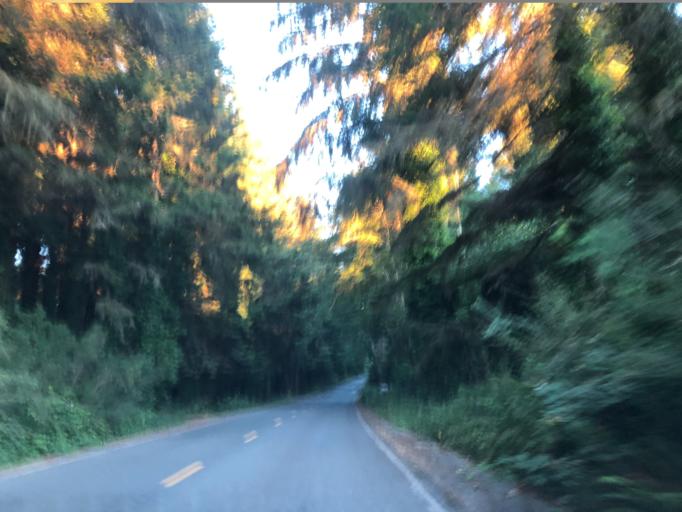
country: US
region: California
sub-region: Humboldt County
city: Westhaven-Moonstone
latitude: 41.0897
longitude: -124.1510
